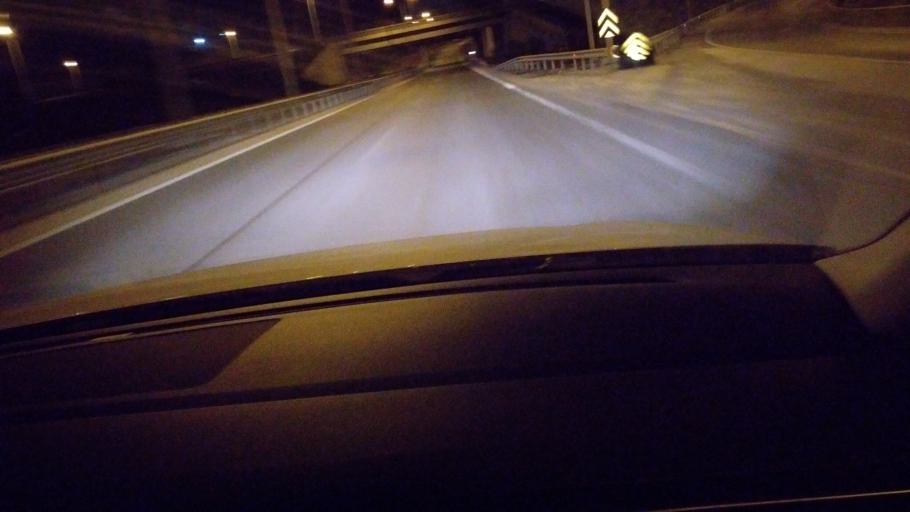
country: TR
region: Ankara
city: Ankara
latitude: 40.0196
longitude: 32.8264
